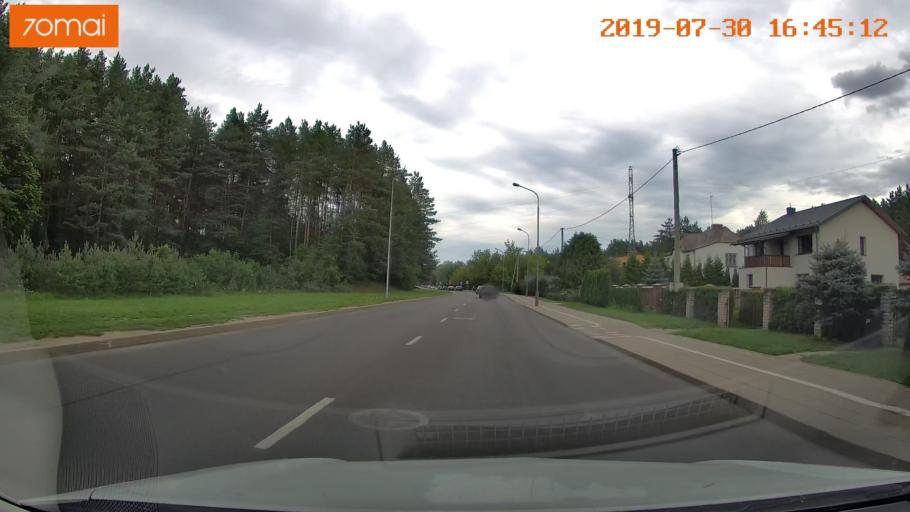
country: LT
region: Vilnius County
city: Rasos
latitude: 54.7263
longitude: 25.3430
